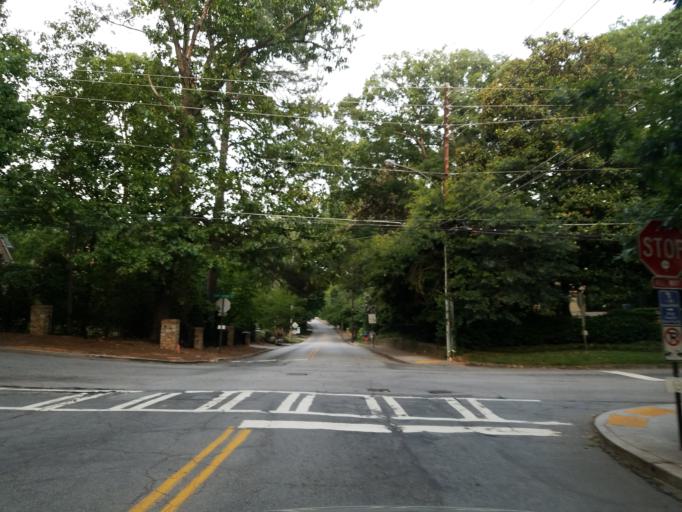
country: US
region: Georgia
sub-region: Fulton County
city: Sandy Springs
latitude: 33.8771
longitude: -84.3876
